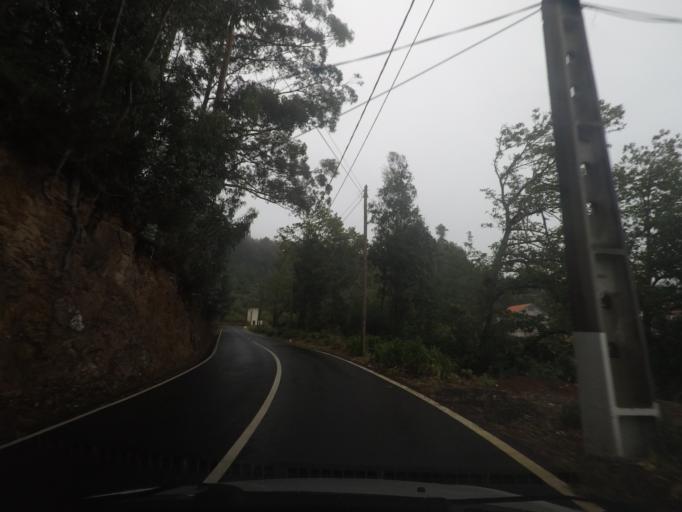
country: PT
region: Madeira
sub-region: Santa Cruz
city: Camacha
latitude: 32.6961
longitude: -16.8383
